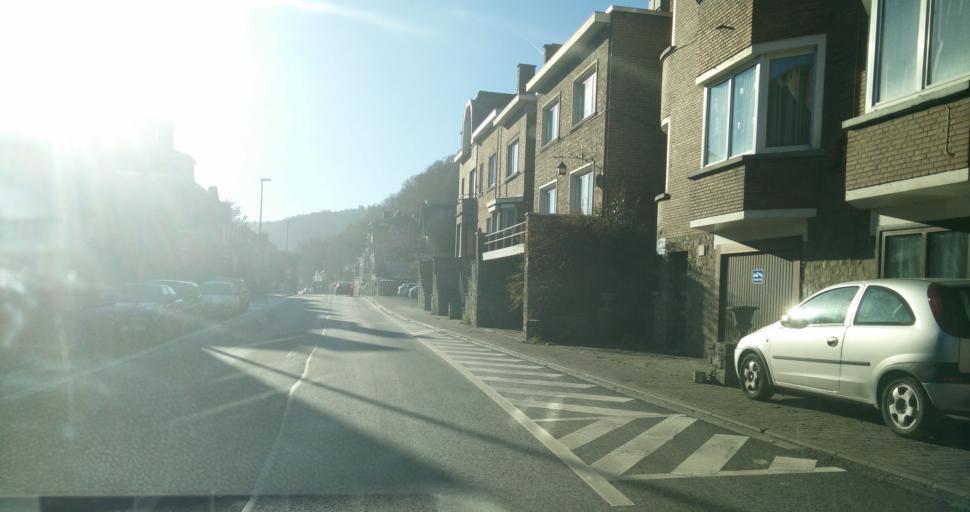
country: BE
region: Wallonia
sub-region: Province de Namur
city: Namur
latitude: 50.4505
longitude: 4.8568
